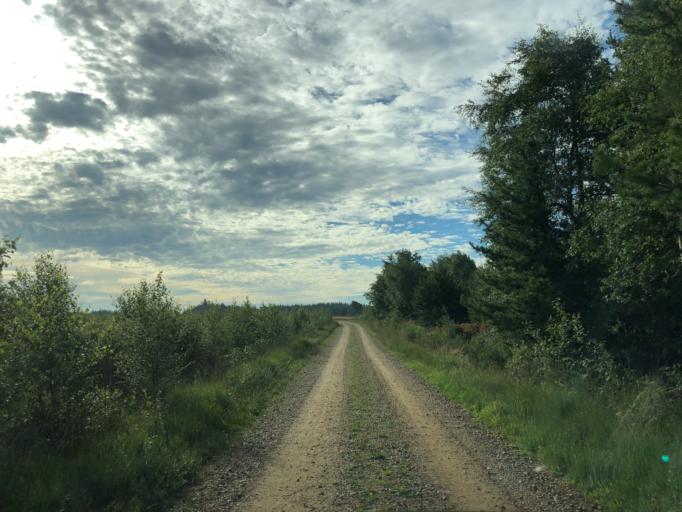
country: DK
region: Central Jutland
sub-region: Holstebro Kommune
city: Ulfborg
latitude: 56.1725
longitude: 8.3755
